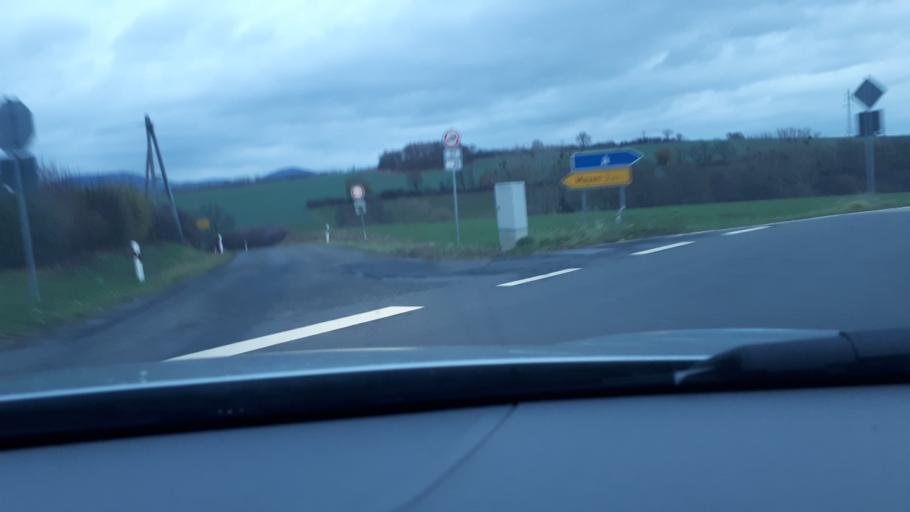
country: DE
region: Rheinland-Pfalz
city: Kehrig
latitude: 50.3040
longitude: 7.2269
